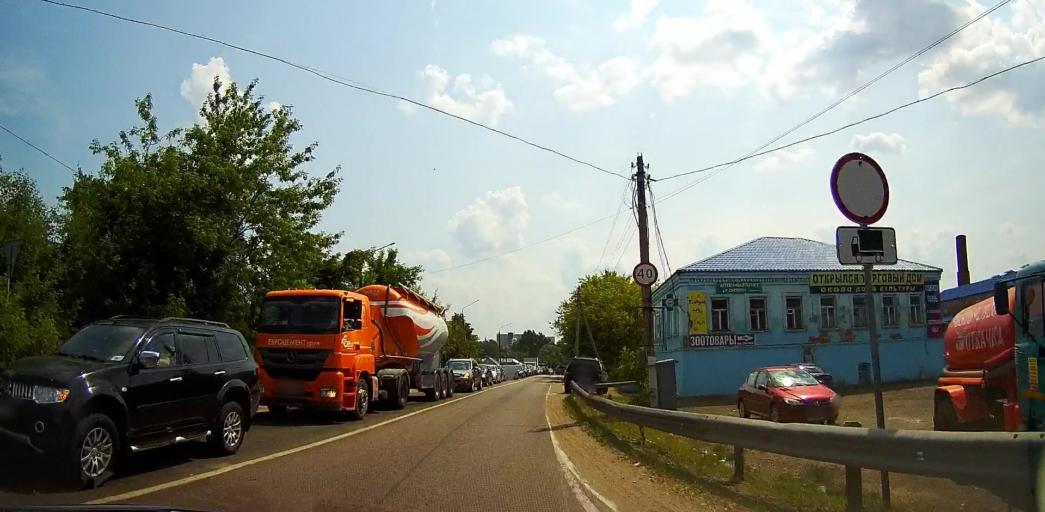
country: RU
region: Moskovskaya
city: Malino
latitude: 55.1128
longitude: 38.1768
